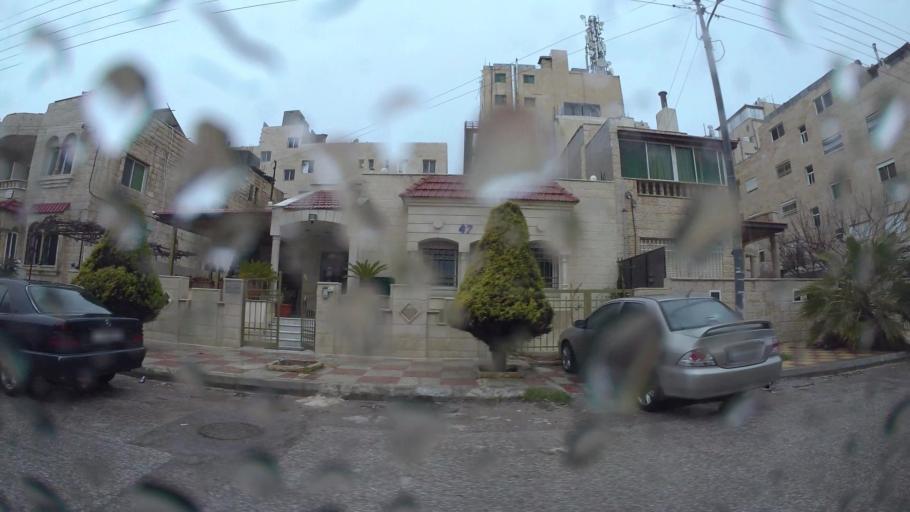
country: JO
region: Amman
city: Al Jubayhah
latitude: 32.0503
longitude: 35.8782
